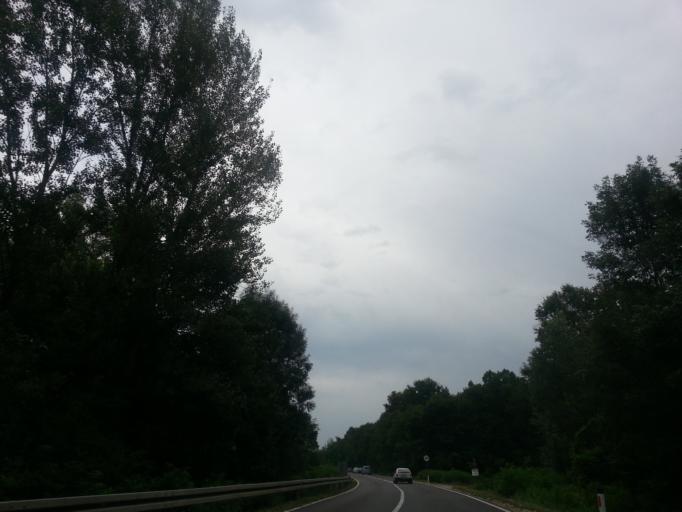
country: HR
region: Vukovarsko-Srijemska
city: Gunja
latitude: 44.8505
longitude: 18.8905
